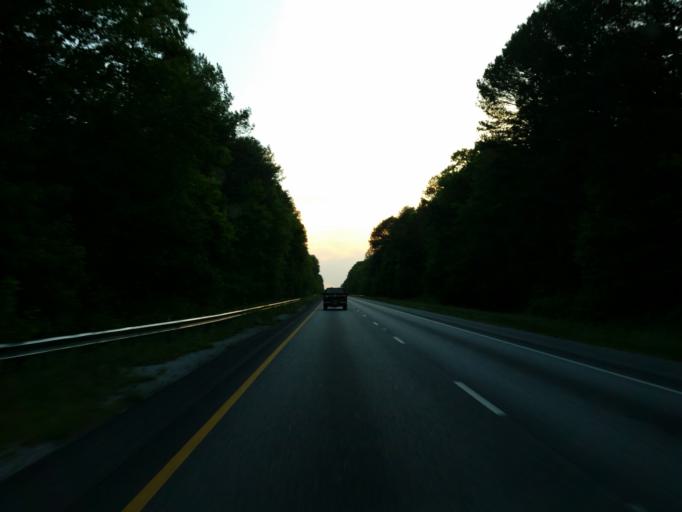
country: US
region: Alabama
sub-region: Cleburne County
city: Heflin
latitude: 33.6198
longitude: -85.6234
